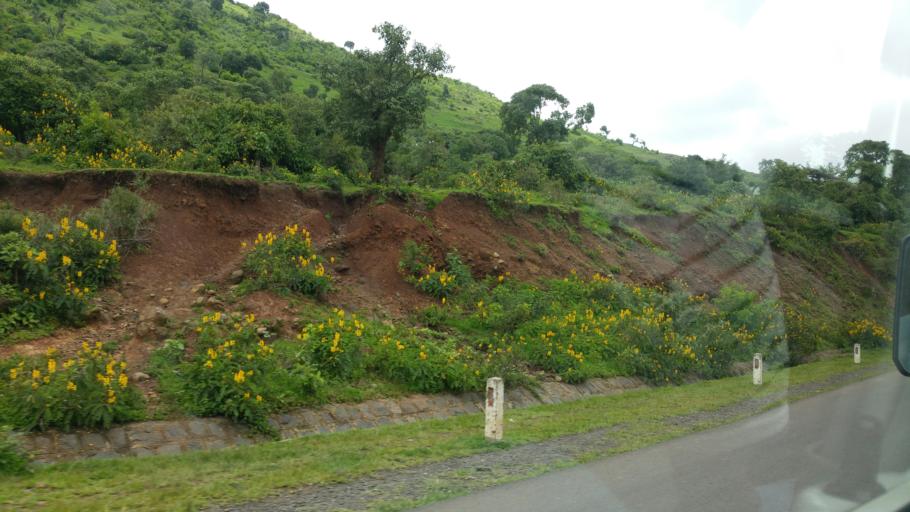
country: ET
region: Amhara
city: Adis Zemen
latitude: 12.1699
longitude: 37.7203
